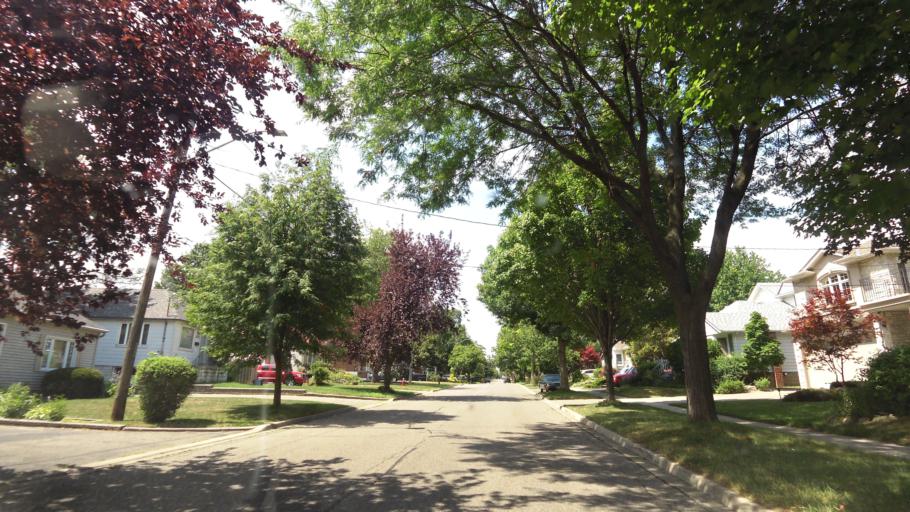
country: CA
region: Ontario
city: Mississauga
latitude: 43.5724
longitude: -79.5822
